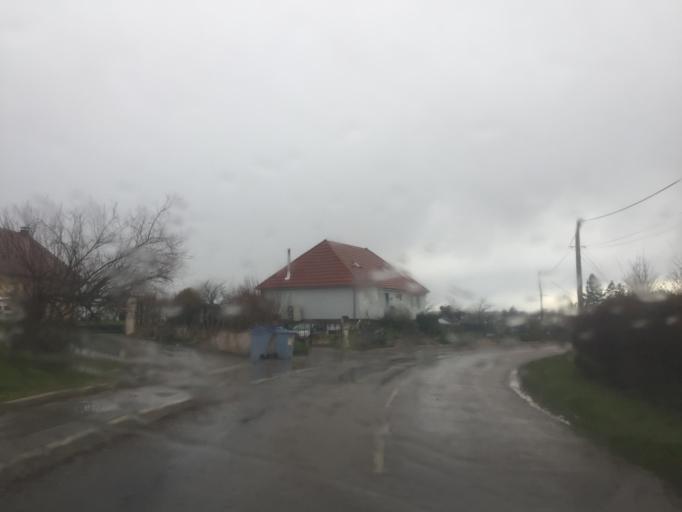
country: FR
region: Franche-Comte
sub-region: Departement du Jura
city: Dampierre
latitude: 47.2130
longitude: 5.7302
